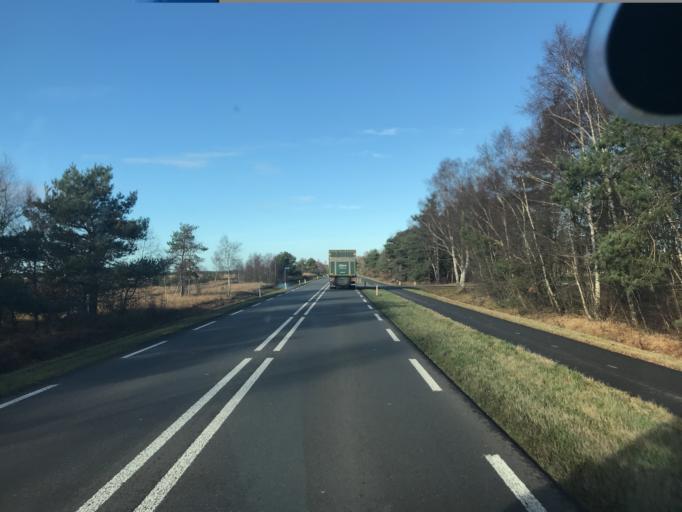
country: NL
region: Gelderland
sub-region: Gemeente Apeldoorn
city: Uddel
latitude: 52.2610
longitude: 5.7421
